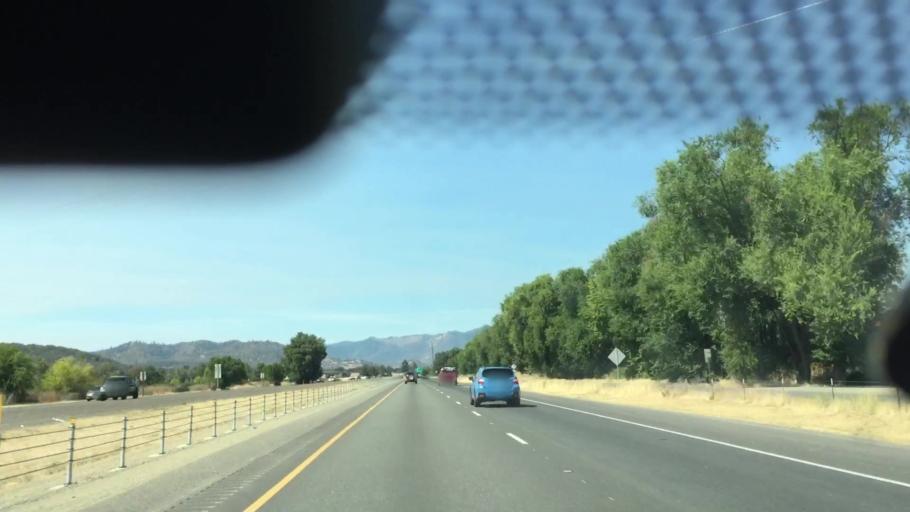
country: US
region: Oregon
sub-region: Jackson County
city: Central Point
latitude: 42.3991
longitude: -122.9311
